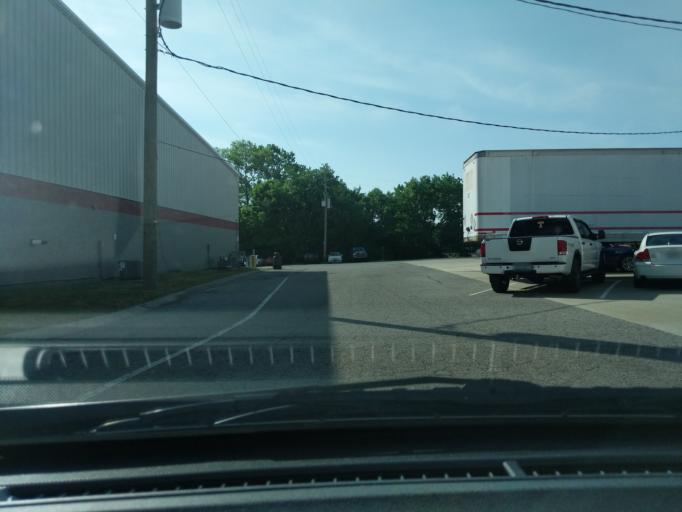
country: US
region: Tennessee
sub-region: Davidson County
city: Oak Hill
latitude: 36.0919
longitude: -86.6902
